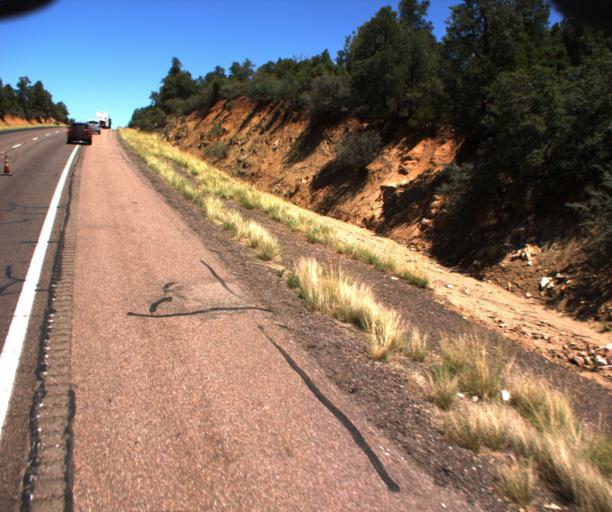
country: US
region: Arizona
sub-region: Gila County
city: Payson
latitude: 34.2029
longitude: -111.3310
